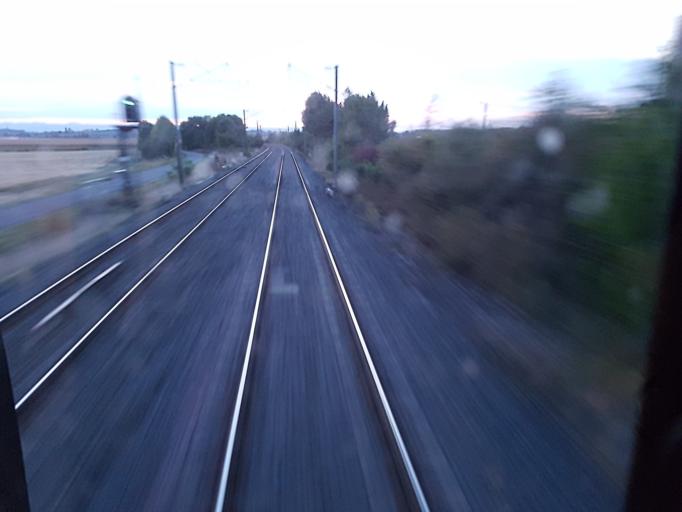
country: FR
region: Auvergne
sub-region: Departement du Puy-de-Dome
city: Randan
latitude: 45.9852
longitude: 3.3056
